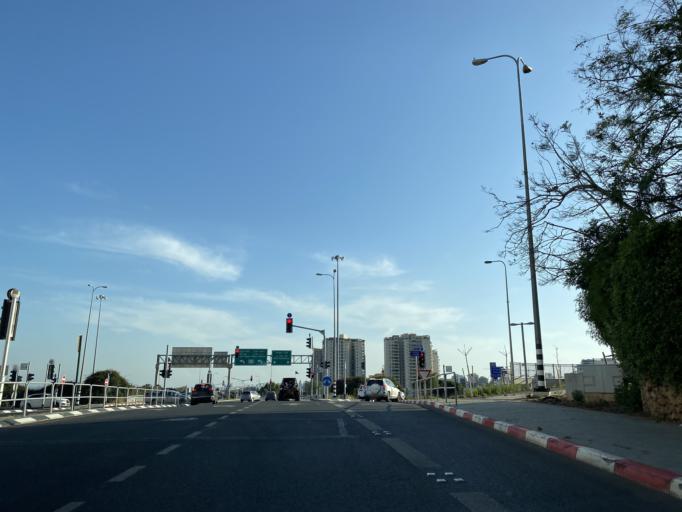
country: IL
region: Central District
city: Kfar Saba
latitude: 32.1698
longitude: 34.9126
